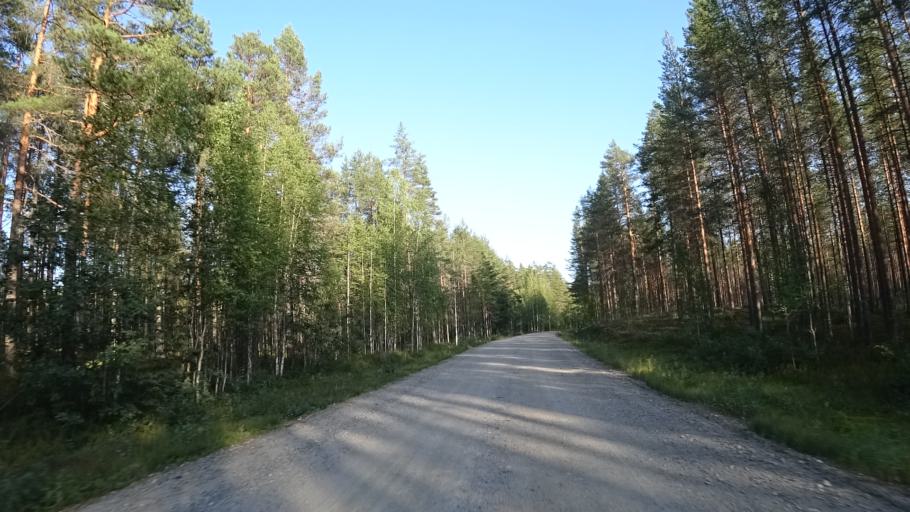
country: FI
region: North Karelia
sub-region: Joensuu
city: Ilomantsi
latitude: 63.1368
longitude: 30.7038
